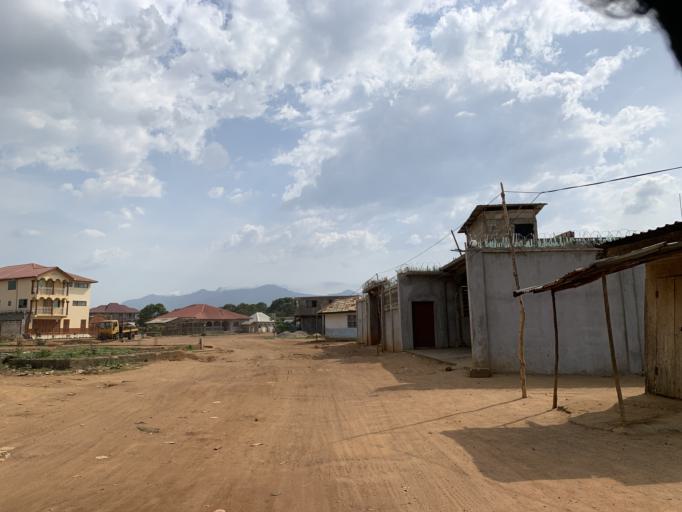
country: SL
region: Western Area
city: Waterloo
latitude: 8.3373
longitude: -13.0410
